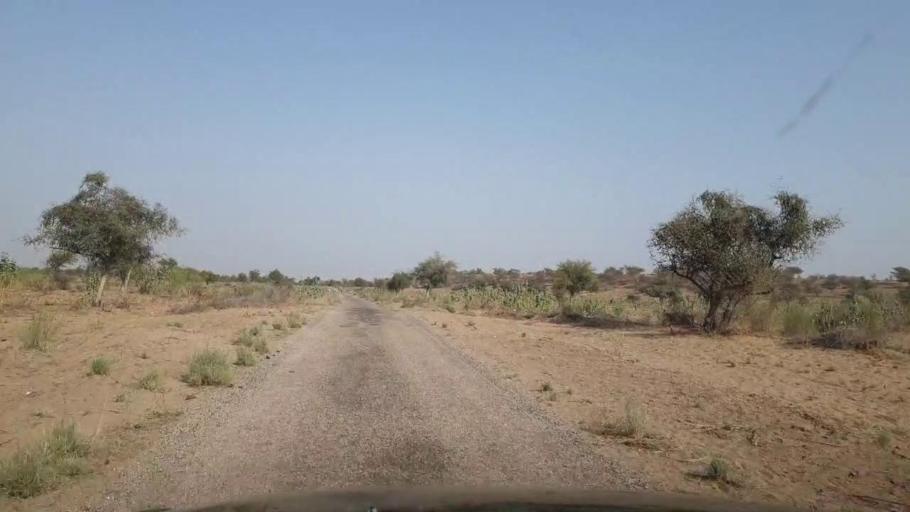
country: PK
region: Sindh
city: Islamkot
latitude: 25.1304
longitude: 70.4892
